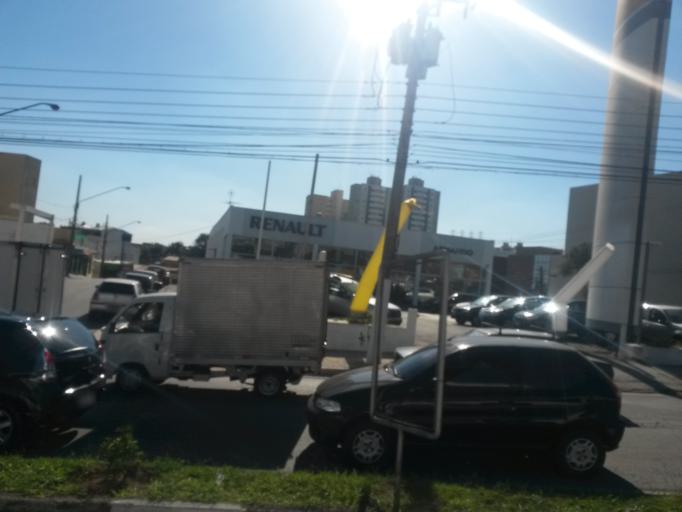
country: BR
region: Sao Paulo
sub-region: Santo Andre
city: Santo Andre
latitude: -23.6799
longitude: -46.5394
